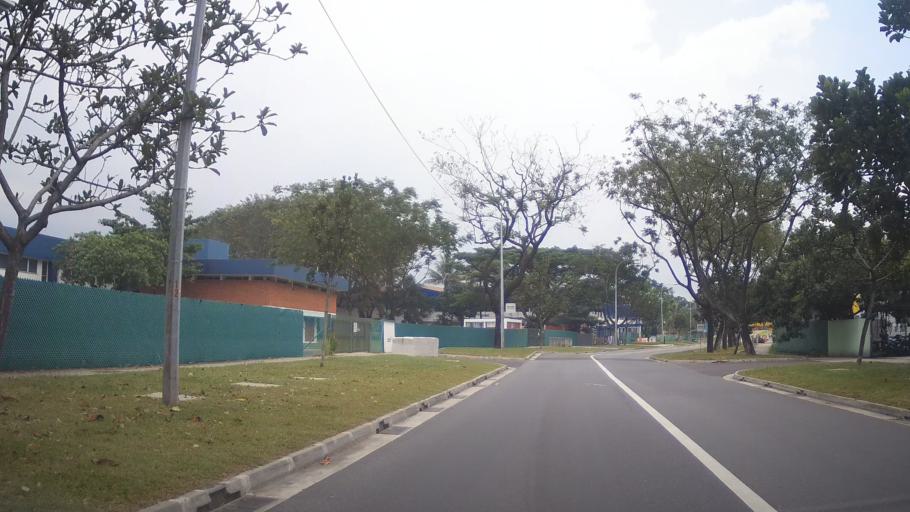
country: MY
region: Johor
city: Johor Bahru
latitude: 1.3333
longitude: 103.7058
